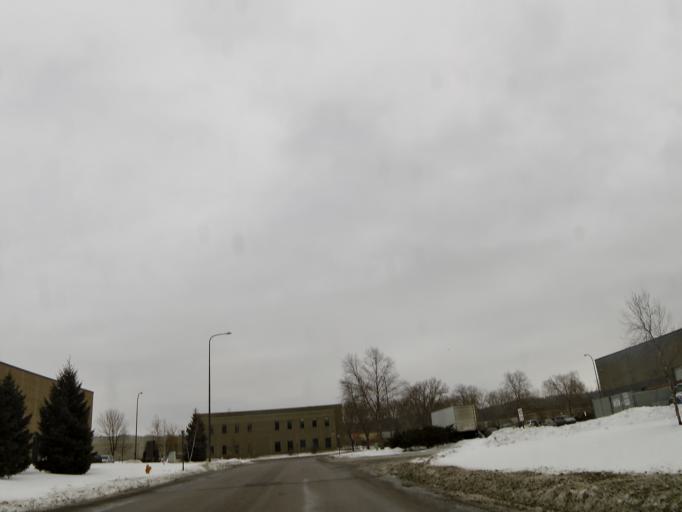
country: US
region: Minnesota
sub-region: Dakota County
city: South Saint Paul
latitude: 44.8902
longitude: -93.0271
